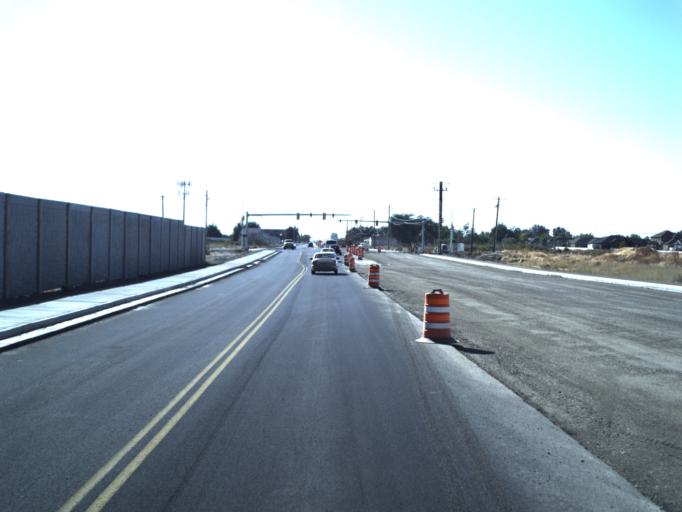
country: US
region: Utah
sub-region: Weber County
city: West Haven
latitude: 41.1906
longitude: -112.0622
